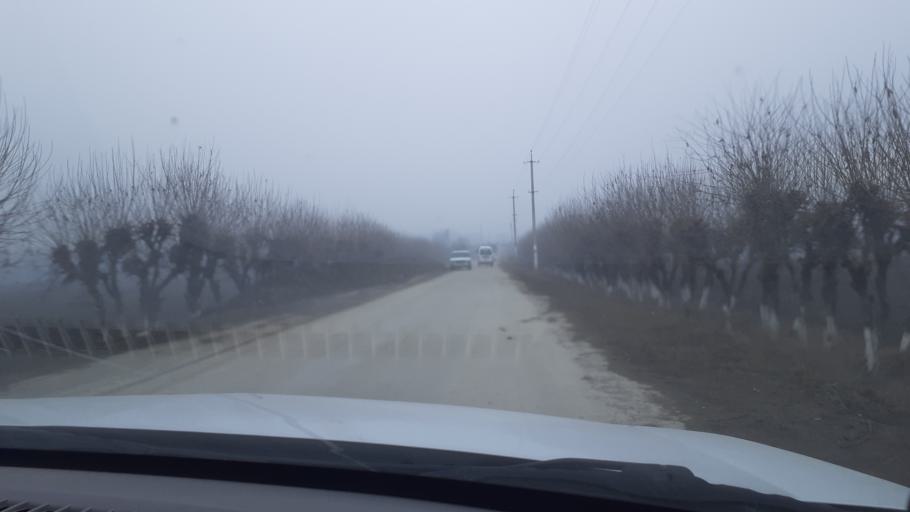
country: UZ
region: Namangan
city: Haqqulobod
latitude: 40.9003
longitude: 71.9998
